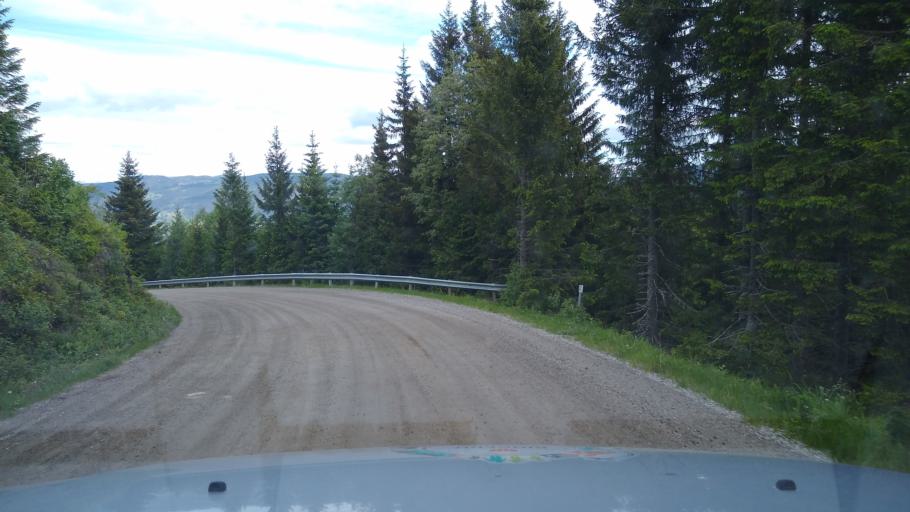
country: NO
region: Oppland
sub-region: Ringebu
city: Ringebu
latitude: 61.4960
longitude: 10.1454
